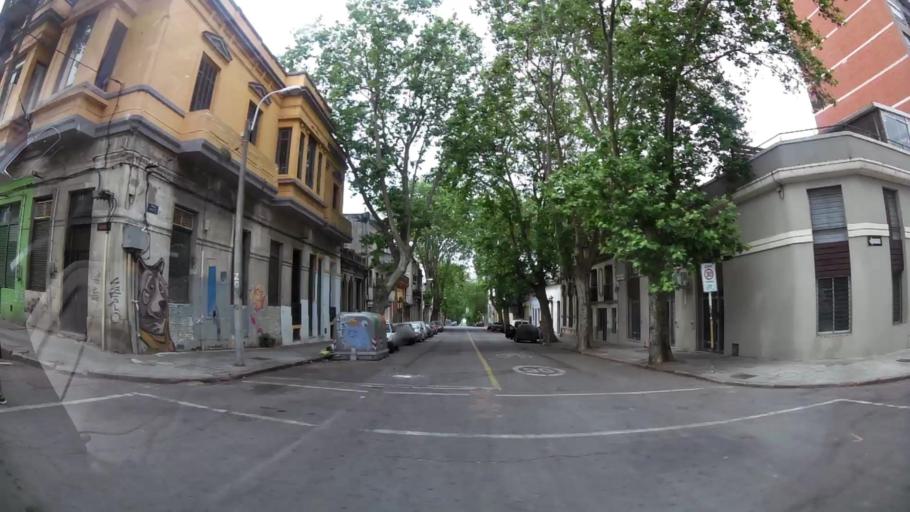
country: UY
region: Montevideo
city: Montevideo
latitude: -34.9100
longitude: -56.1819
